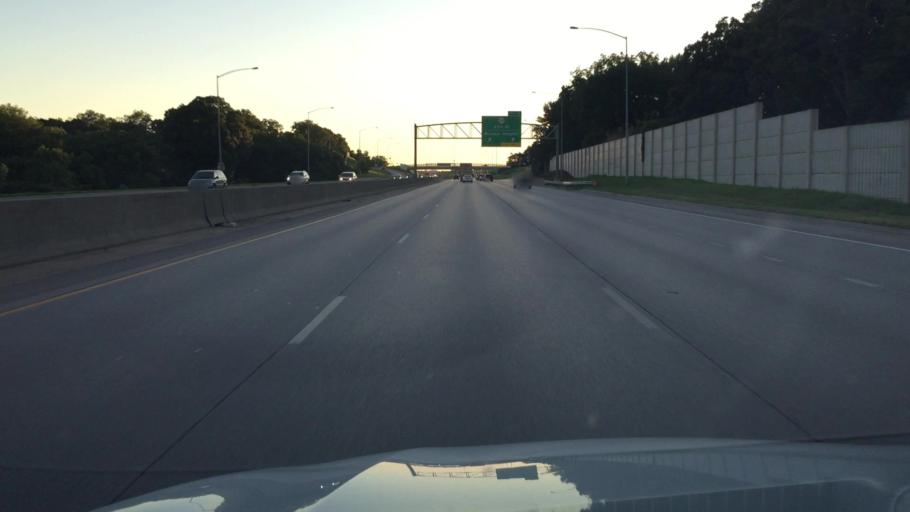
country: US
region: Iowa
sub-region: Polk County
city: Windsor Heights
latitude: 41.5927
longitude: -93.6967
